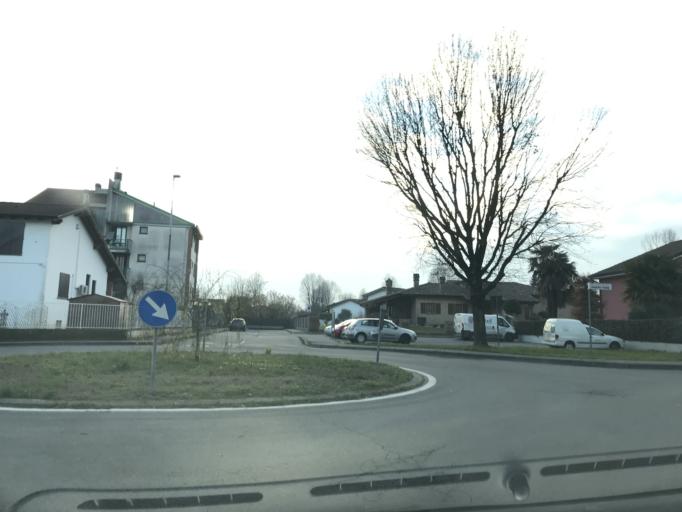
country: IT
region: Lombardy
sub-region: Provincia di Lodi
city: Muzza di Cornegliano Laudense
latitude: 45.2795
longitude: 9.4673
